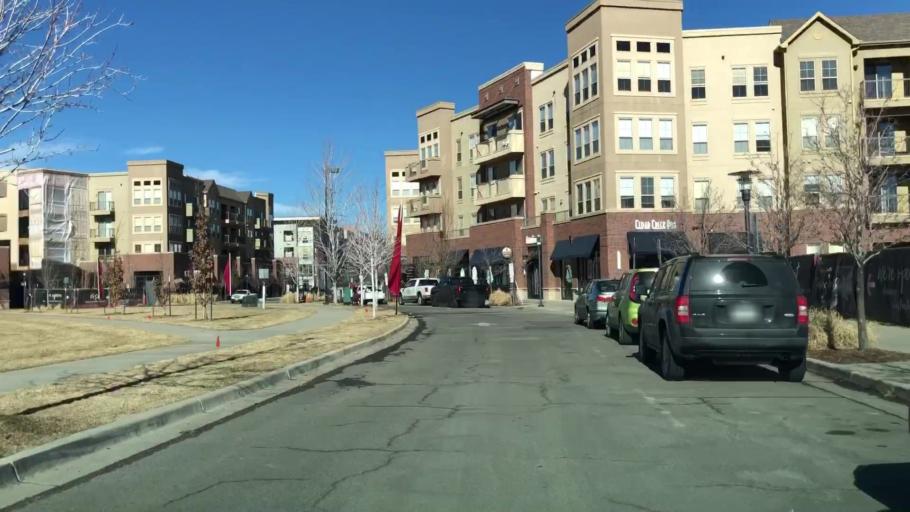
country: US
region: Colorado
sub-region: Adams County
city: Aurora
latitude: 39.7478
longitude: -104.8372
